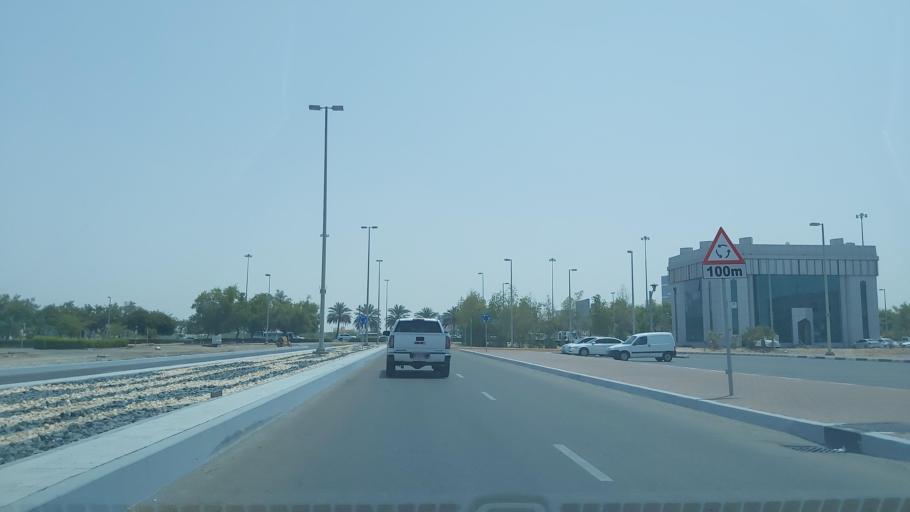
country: AE
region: Abu Dhabi
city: Abu Dhabi
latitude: 24.3779
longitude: 54.5225
